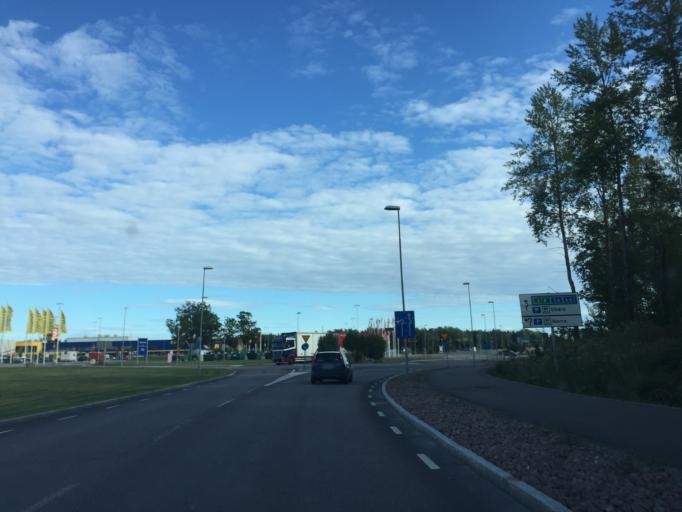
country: SE
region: Vaestmanland
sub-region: Vasteras
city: Vasteras
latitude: 59.6088
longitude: 16.4479
